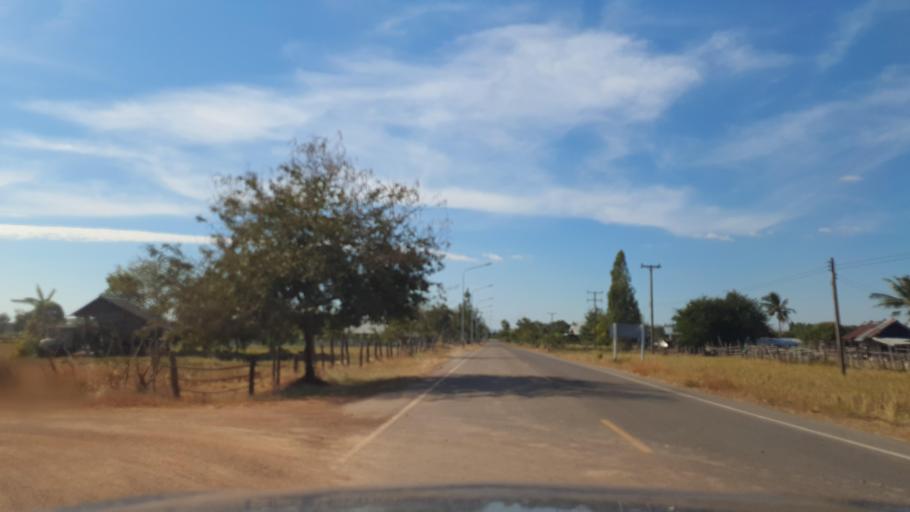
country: TH
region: Kalasin
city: Khao Wong
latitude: 16.6473
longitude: 104.1611
